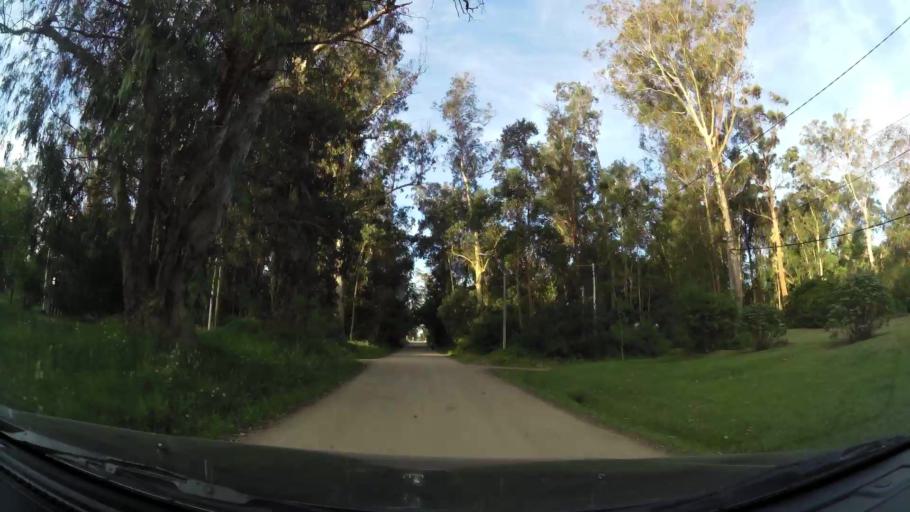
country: UY
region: Canelones
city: Atlantida
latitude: -34.7702
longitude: -55.8041
